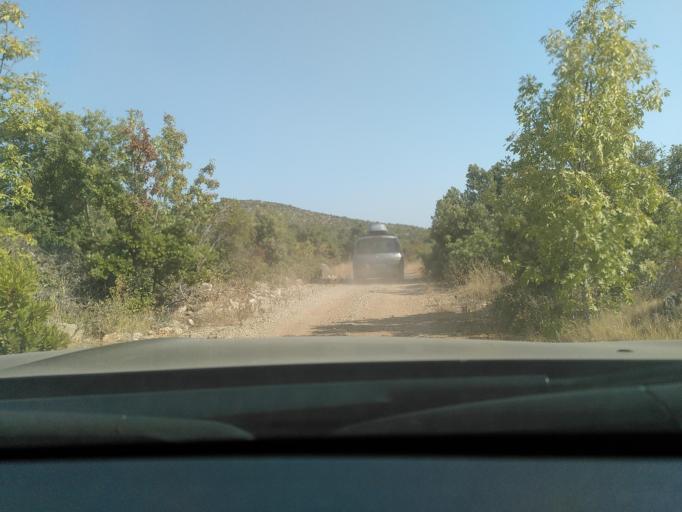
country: HR
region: Splitsko-Dalmatinska
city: Stari Grad
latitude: 43.1616
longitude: 16.5543
